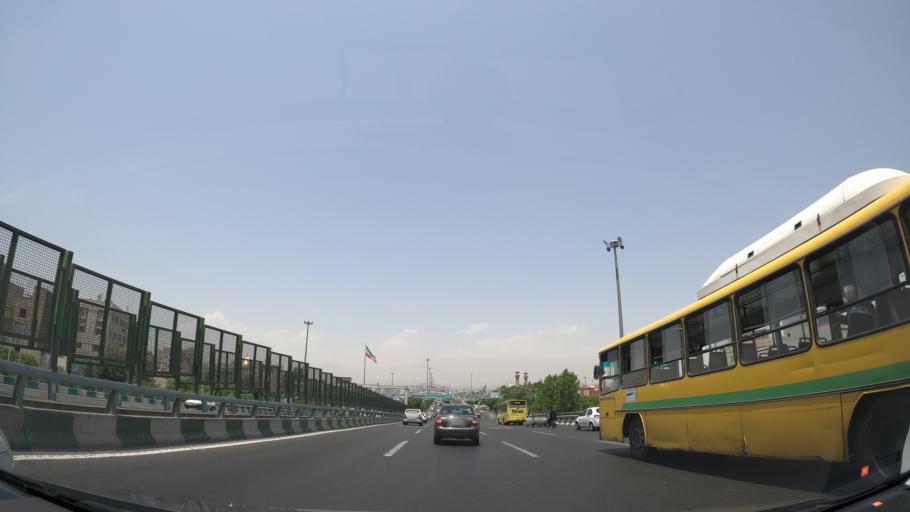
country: IR
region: Tehran
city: Tehran
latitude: 35.6605
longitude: 51.3822
